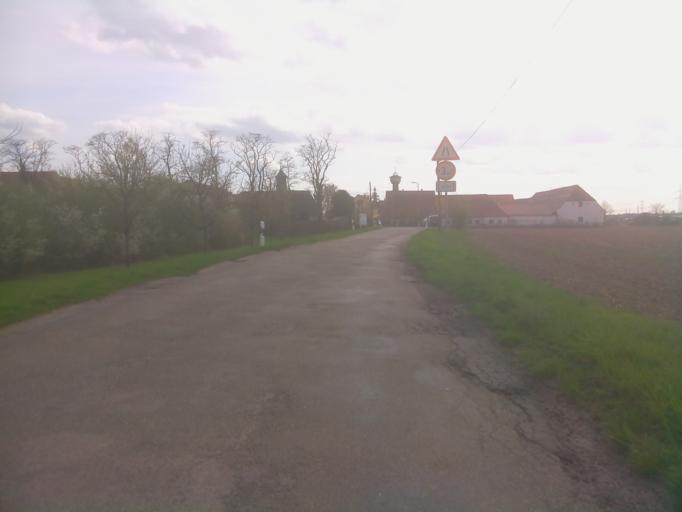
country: DE
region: Hesse
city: Viernheim
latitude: 49.5153
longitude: 8.5778
